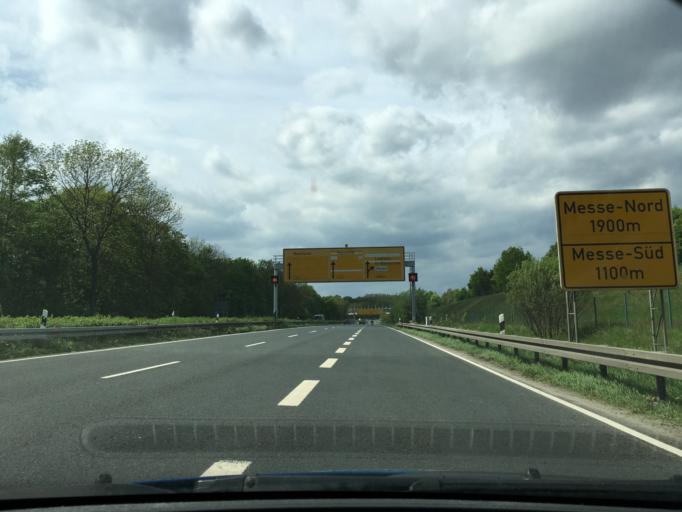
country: DE
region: Lower Saxony
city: Laatzen
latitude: 52.3089
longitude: 9.8229
